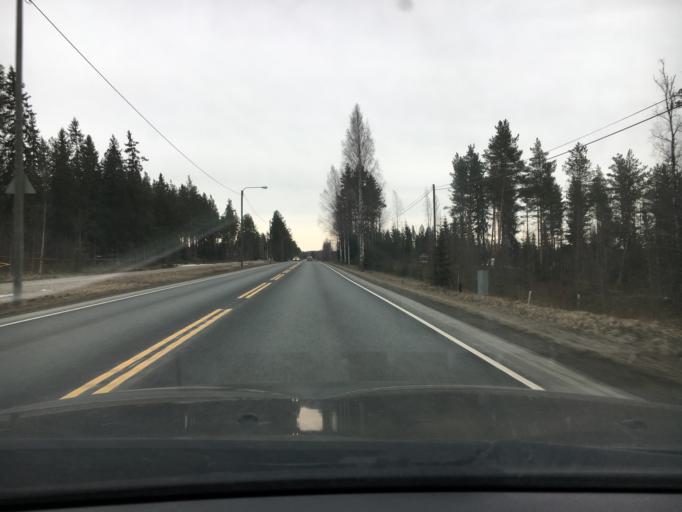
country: FI
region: Northern Savo
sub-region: Kuopio
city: Siilinjaervi
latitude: 63.1002
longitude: 27.6487
